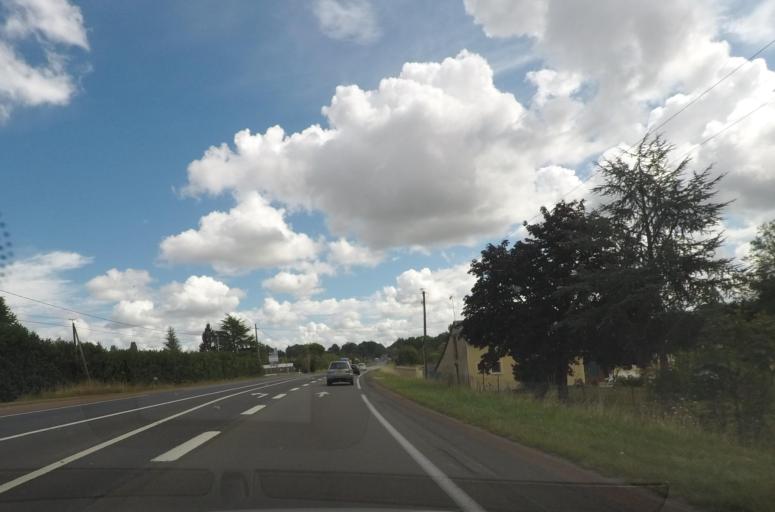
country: FR
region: Pays de la Loire
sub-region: Departement de la Sarthe
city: Clermont-Creans
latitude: 47.7121
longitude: -0.0355
